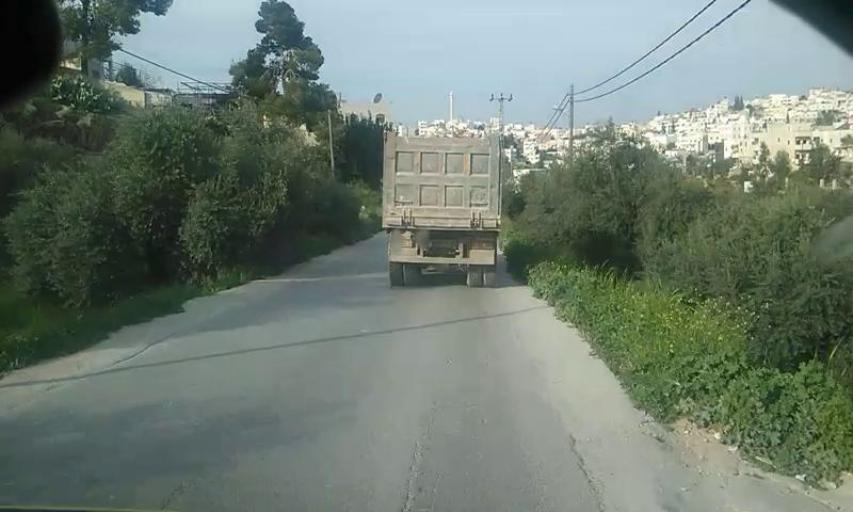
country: PS
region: West Bank
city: Bayt Ula
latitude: 31.5904
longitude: 35.0257
